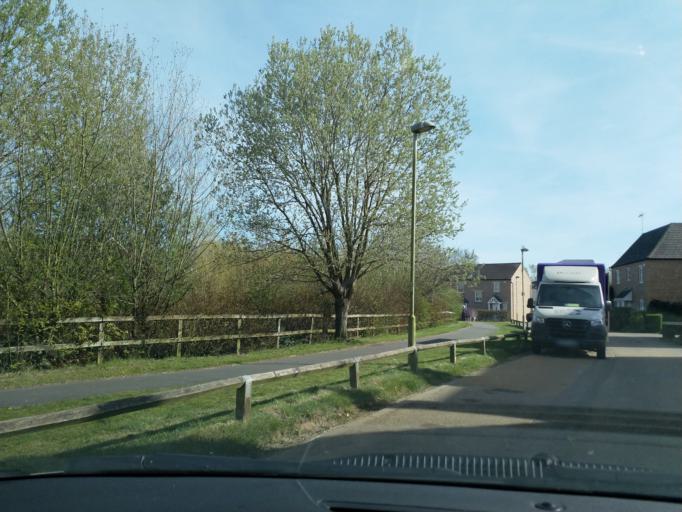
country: GB
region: England
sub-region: Oxfordshire
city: Banbury
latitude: 52.0809
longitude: -1.3416
